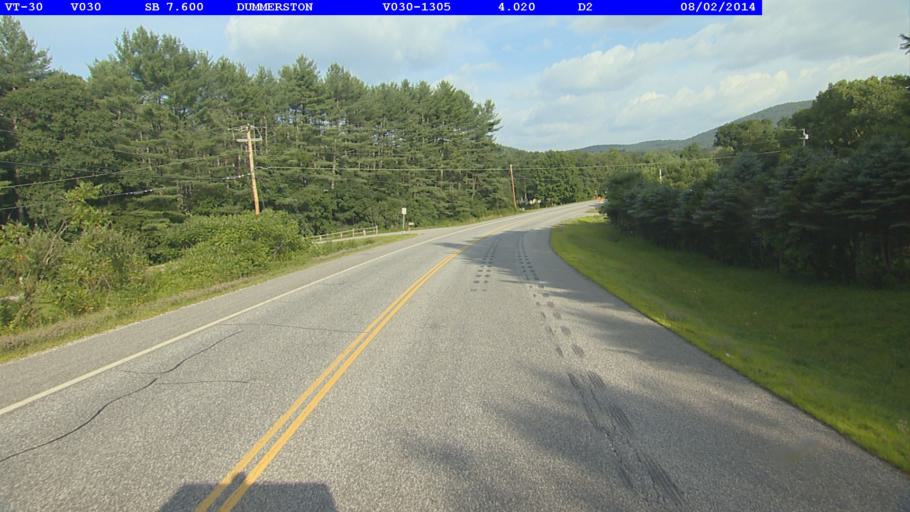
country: US
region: Vermont
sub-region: Windham County
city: Newfane
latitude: 42.9489
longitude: -72.6208
